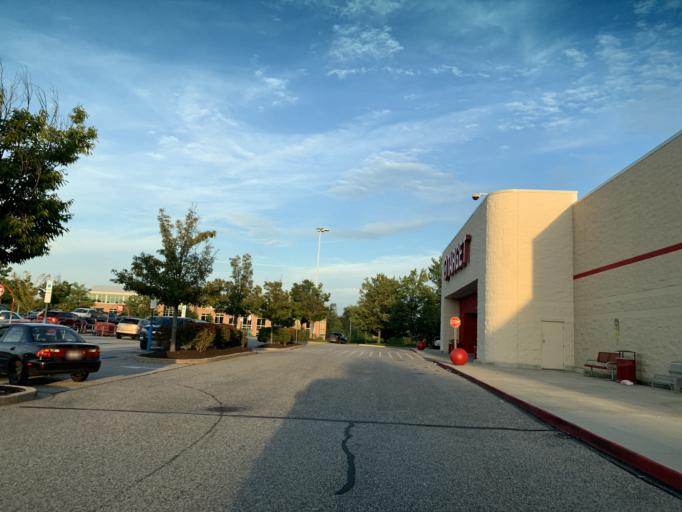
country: US
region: Maryland
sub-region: Harford County
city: Aberdeen
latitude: 39.5213
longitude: -76.1784
